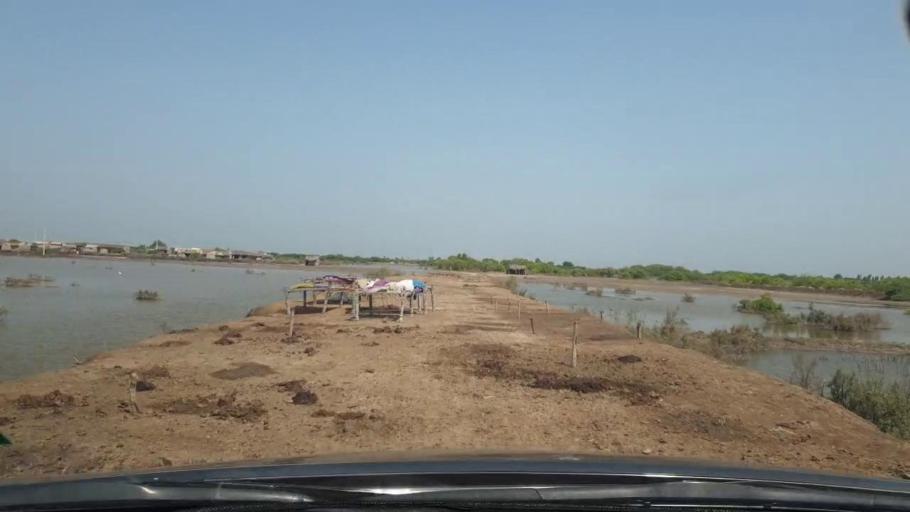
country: PK
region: Sindh
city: Tando Bago
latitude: 24.8121
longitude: 69.1120
